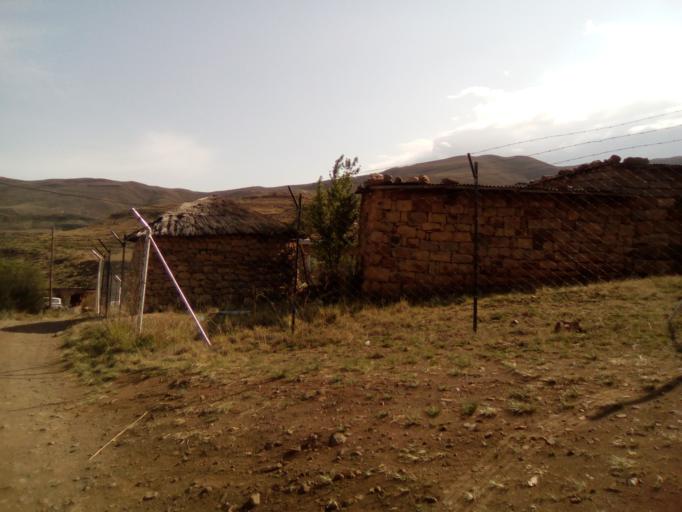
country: LS
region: Qacha's Nek
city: Qacha's Nek
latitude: -30.0973
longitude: 28.6501
